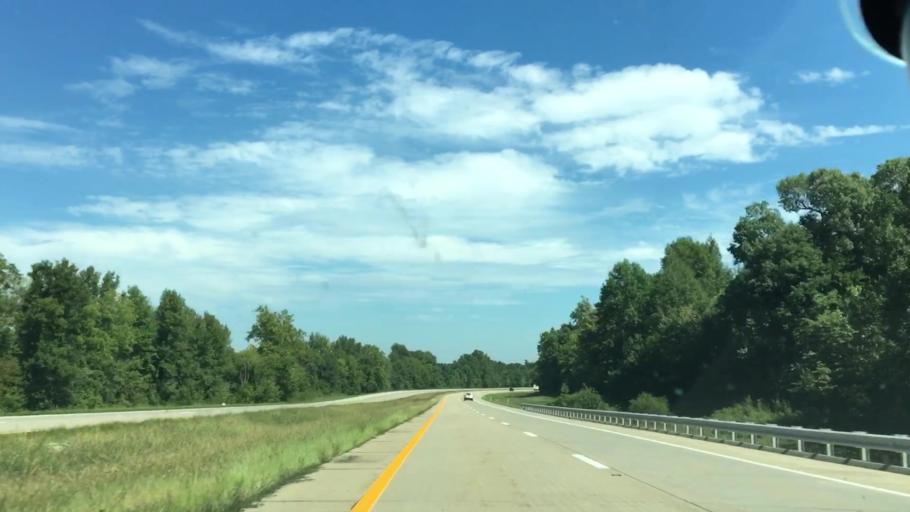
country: US
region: Indiana
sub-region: Warrick County
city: Newburgh
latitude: 37.7621
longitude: -87.3194
